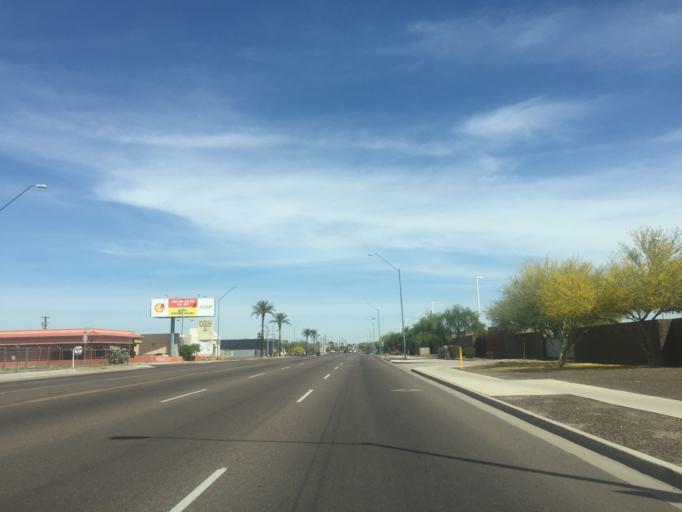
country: US
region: Arizona
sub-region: Maricopa County
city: Phoenix
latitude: 33.4325
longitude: -112.0477
